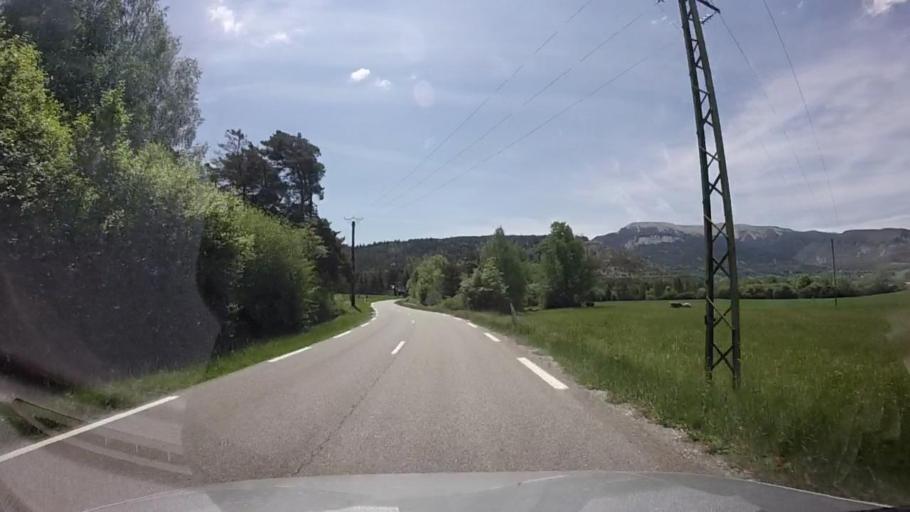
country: FR
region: Provence-Alpes-Cote d'Azur
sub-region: Departement des Alpes-de-Haute-Provence
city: Seyne-les-Alpes
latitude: 44.3808
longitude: 6.3267
